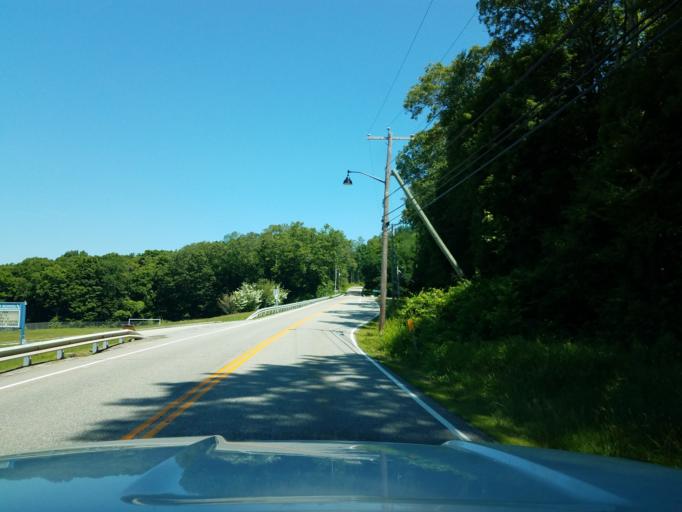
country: US
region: Connecticut
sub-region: New London County
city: Baltic
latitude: 41.6232
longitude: -72.0847
